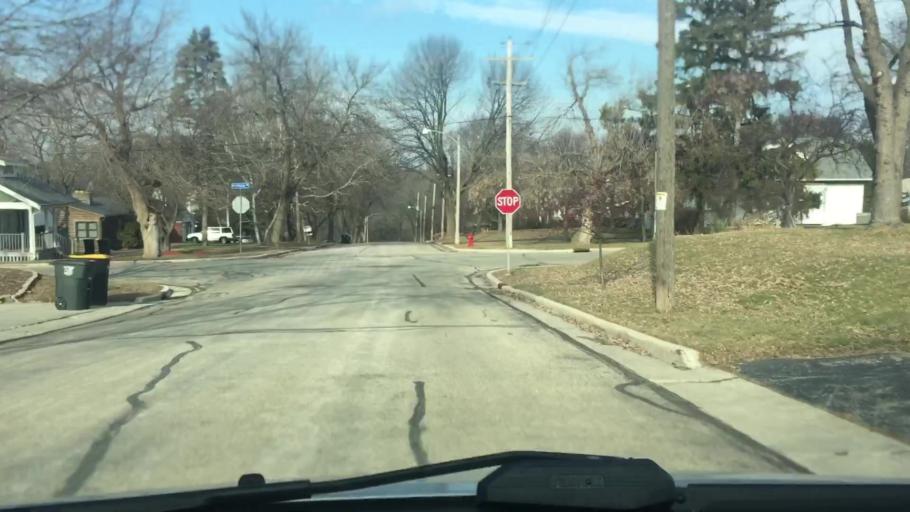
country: US
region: Wisconsin
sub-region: Waukesha County
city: Elm Grove
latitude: 43.0398
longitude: -88.0582
